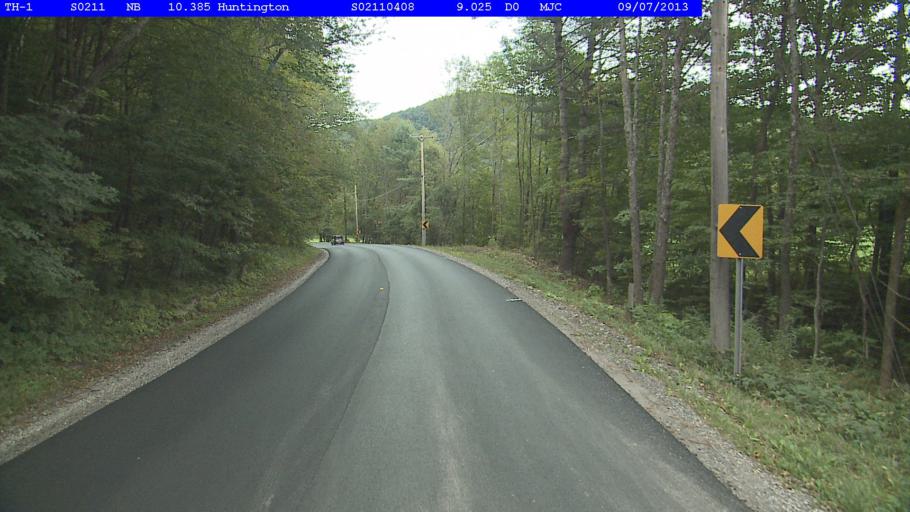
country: US
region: Vermont
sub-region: Chittenden County
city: Hinesburg
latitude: 44.3441
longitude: -72.9940
